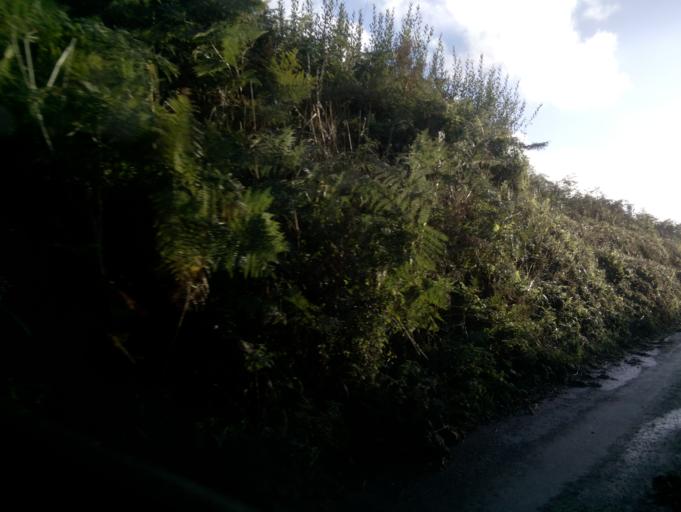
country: GB
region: England
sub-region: Devon
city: Totnes
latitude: 50.3458
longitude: -3.6710
